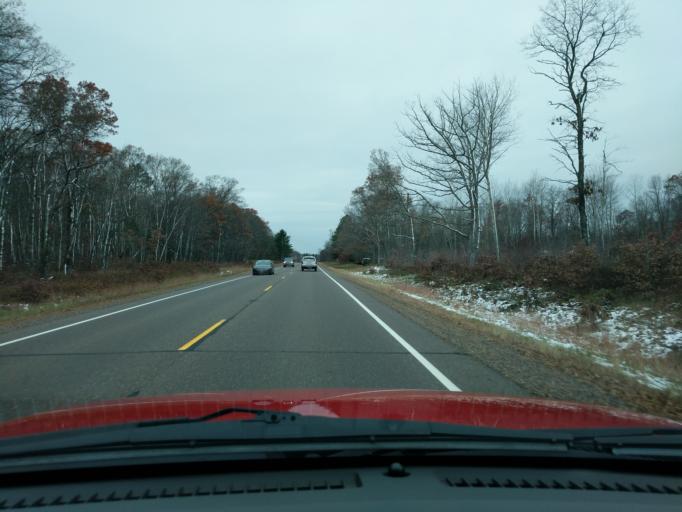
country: US
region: Wisconsin
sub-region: Washburn County
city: Shell Lake
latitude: 45.8132
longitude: -92.1368
